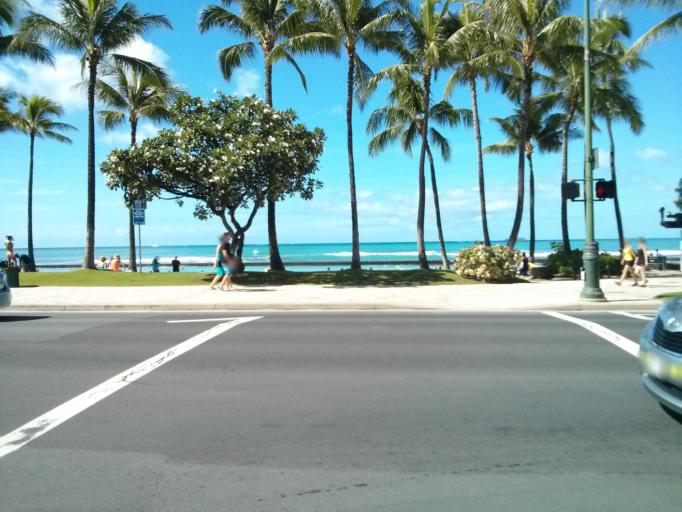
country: US
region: Hawaii
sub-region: Honolulu County
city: Honolulu
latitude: 21.2726
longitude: -157.8232
